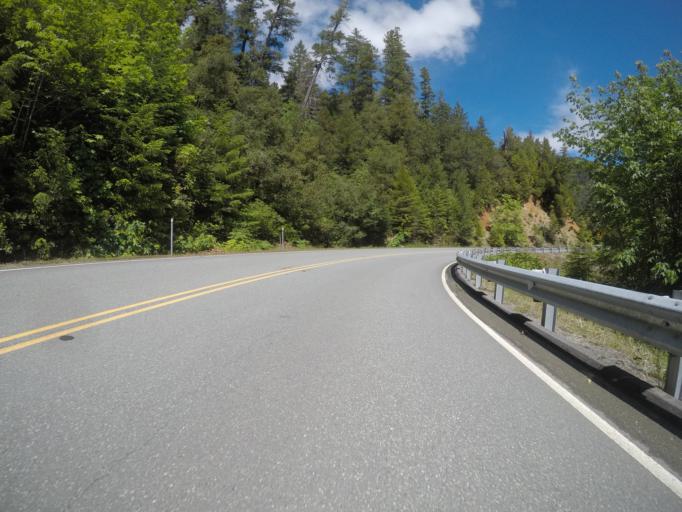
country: US
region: California
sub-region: Del Norte County
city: Bertsch-Oceanview
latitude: 41.7193
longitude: -123.9477
